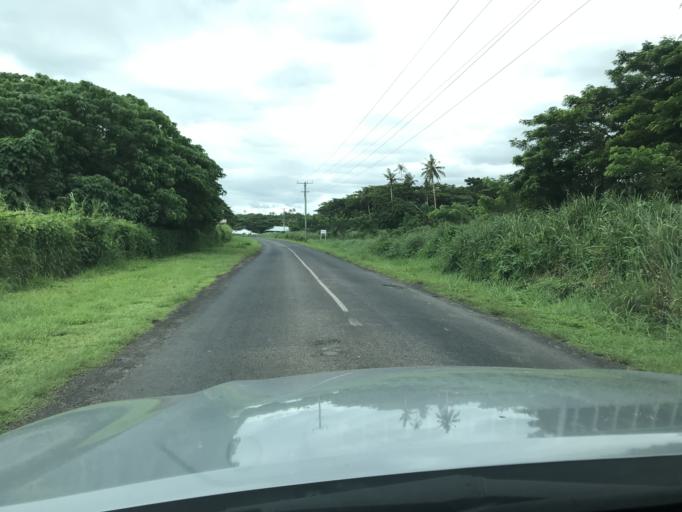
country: WS
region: Aiga-i-le-Tai
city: Mulifanua
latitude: -13.8313
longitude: -172.0330
